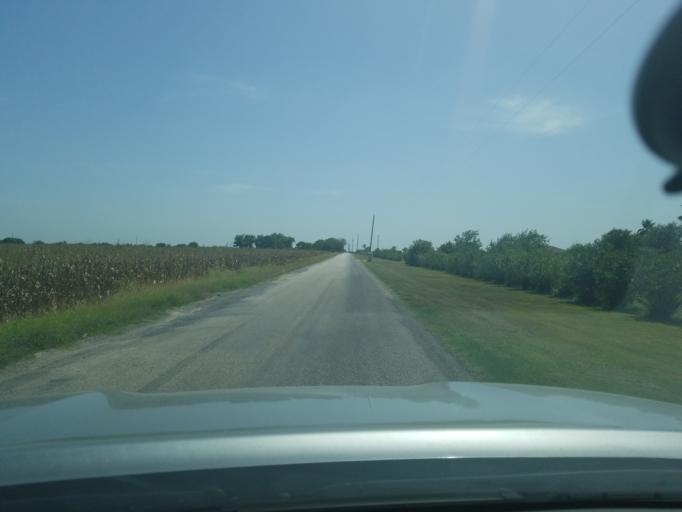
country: US
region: Texas
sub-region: Guadalupe County
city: Lake Dunlap
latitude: 29.6750
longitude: -98.0229
